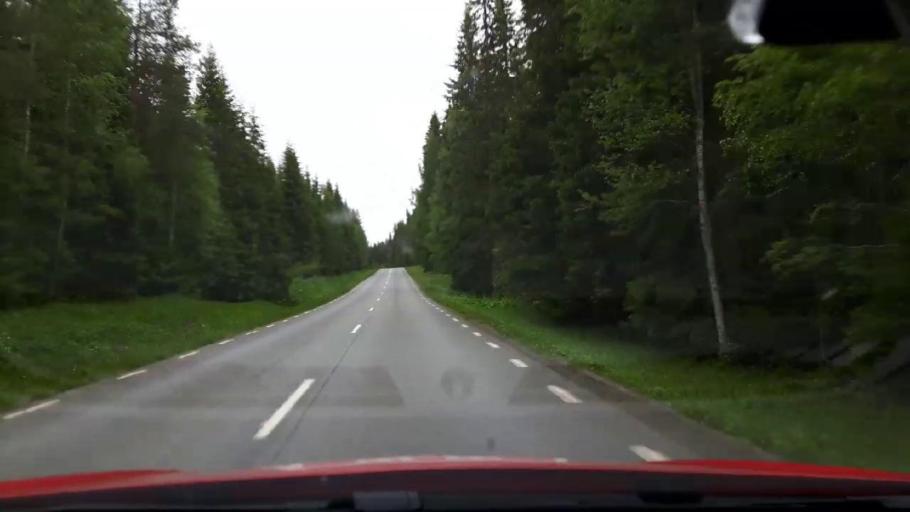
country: SE
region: Jaemtland
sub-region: Stroemsunds Kommun
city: Stroemsund
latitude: 63.4626
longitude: 15.4567
